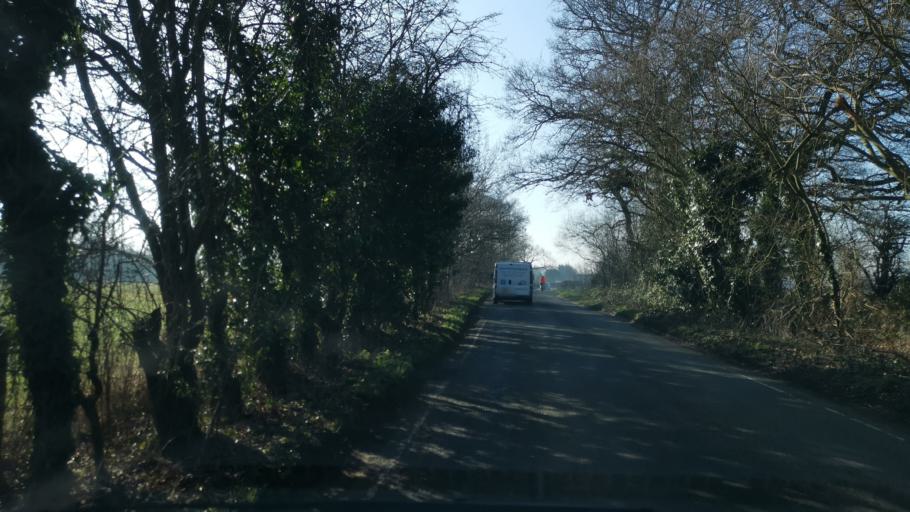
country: GB
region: England
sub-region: City of York
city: Murton
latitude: 53.9816
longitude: -1.0089
